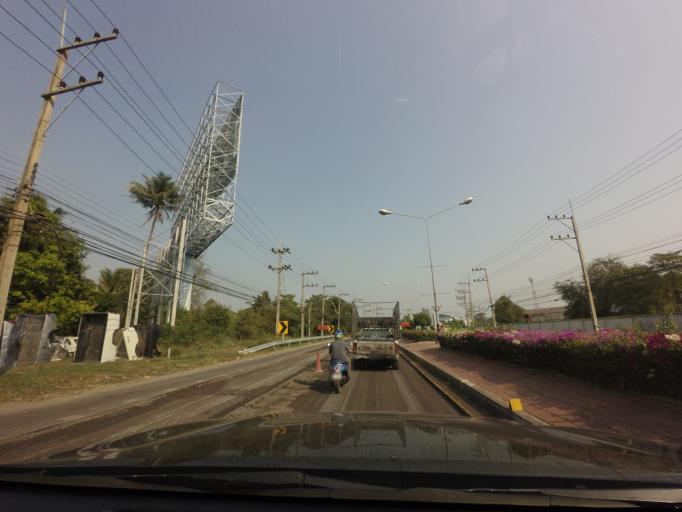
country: TH
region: Kanchanaburi
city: Tha Maka
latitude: 13.8989
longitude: 99.7921
